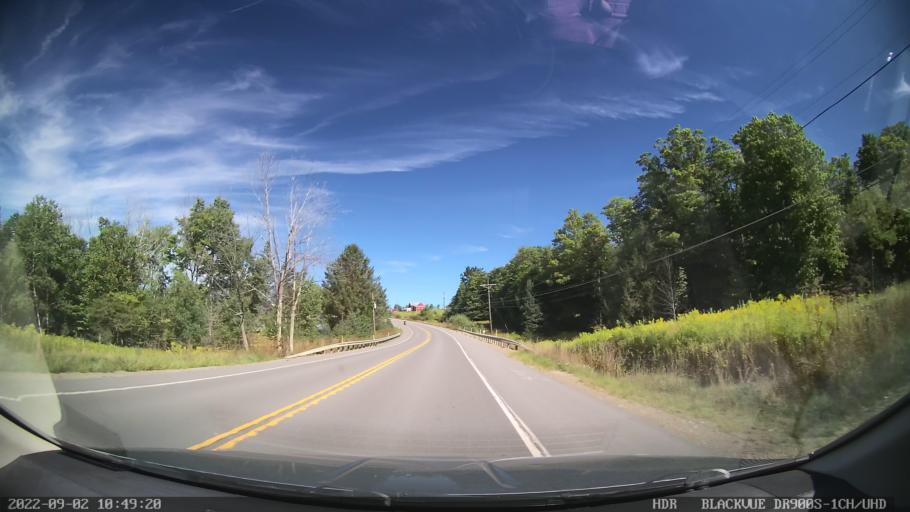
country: US
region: Pennsylvania
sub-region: Tioga County
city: Blossburg
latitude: 41.5990
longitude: -77.1108
